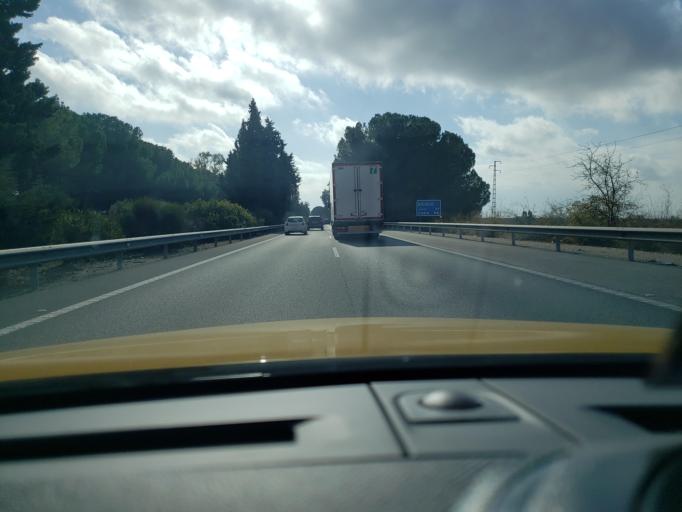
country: ES
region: Andalusia
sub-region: Provincia de Sevilla
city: Dos Hermanas
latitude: 37.2266
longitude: -5.9107
